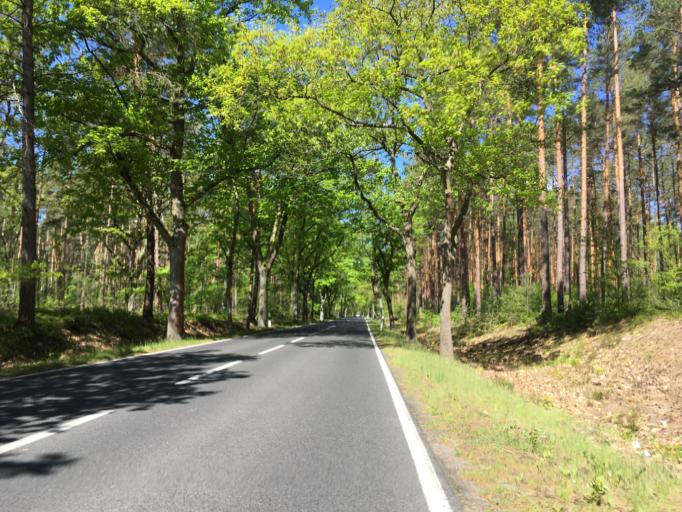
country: DE
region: Brandenburg
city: Birkenwerder
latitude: 52.7193
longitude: 13.3366
